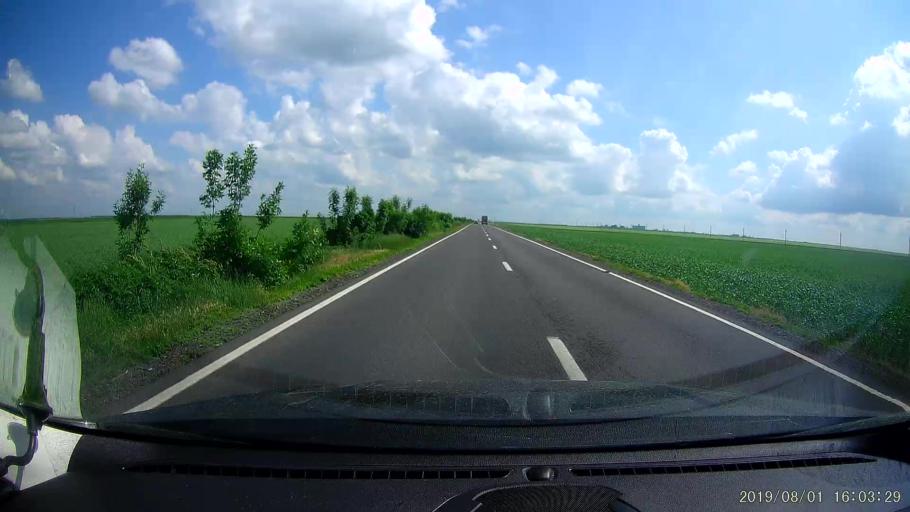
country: RO
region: Calarasi
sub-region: Comuna Dragalina
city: Drajna Noua
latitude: 44.4708
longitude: 27.3842
